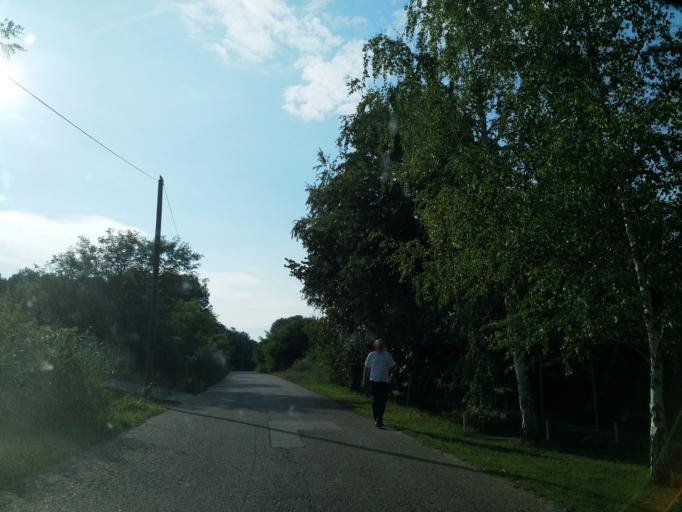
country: RS
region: Central Serbia
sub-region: Pomoravski Okrug
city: Jagodina
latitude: 43.9824
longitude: 21.2235
